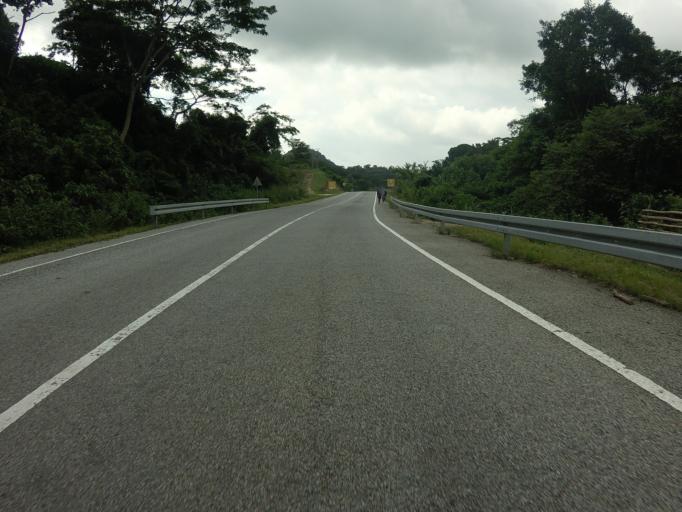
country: GH
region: Volta
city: Kpandu
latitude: 6.8352
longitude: 0.4191
